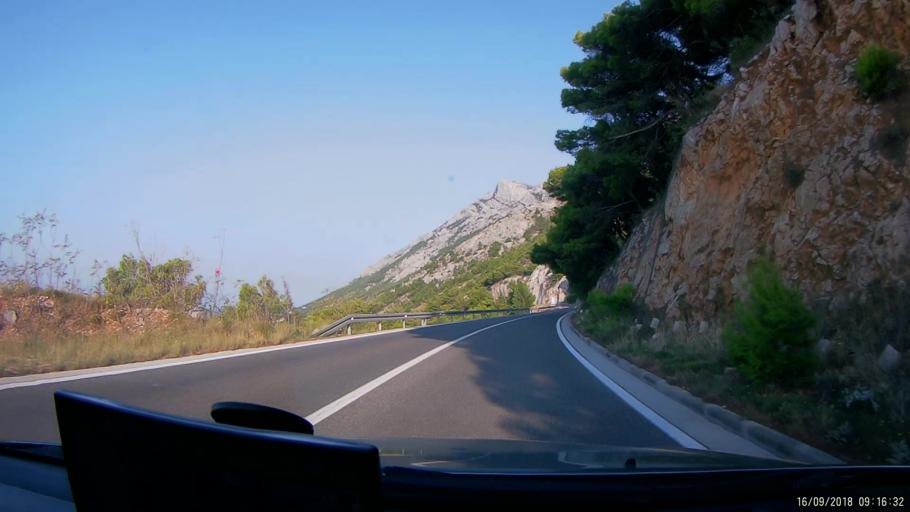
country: HR
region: Splitsko-Dalmatinska
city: Donja Brela
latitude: 43.4007
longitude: 16.8661
